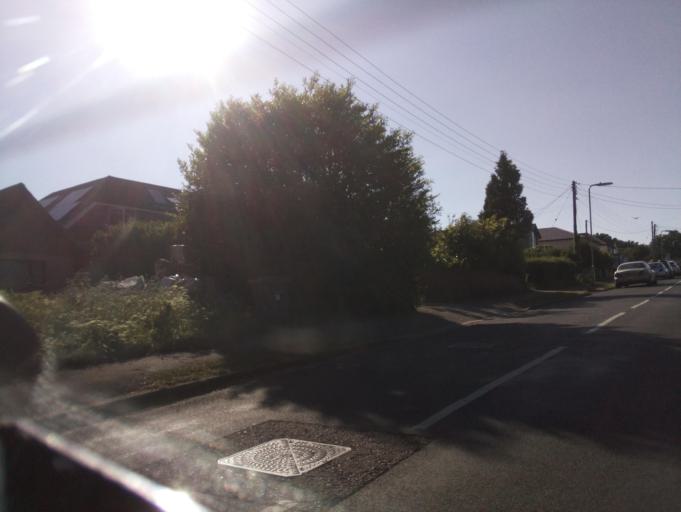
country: GB
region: England
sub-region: Hampshire
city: Eastleigh
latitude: 50.9905
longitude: -1.3474
